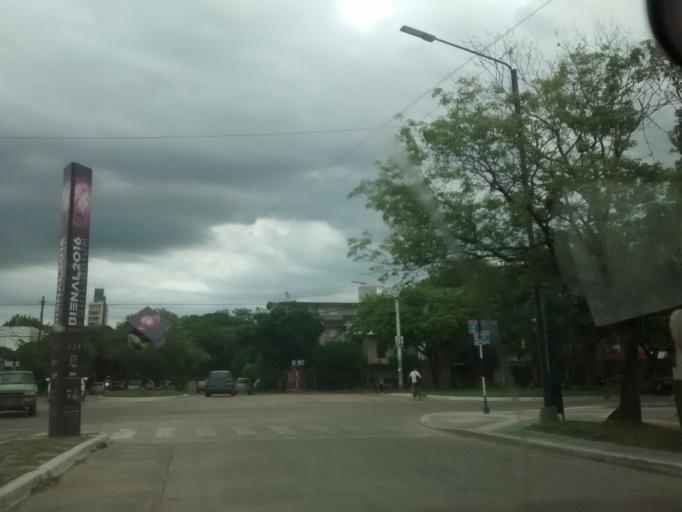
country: AR
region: Chaco
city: Resistencia
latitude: -27.4407
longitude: -58.9836
